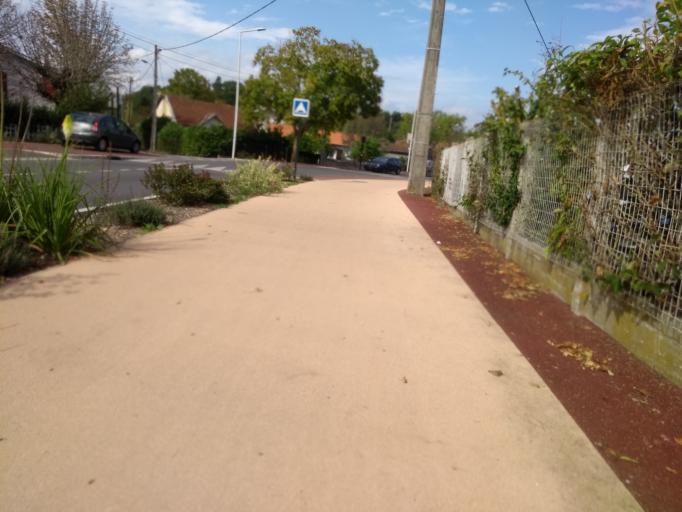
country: FR
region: Aquitaine
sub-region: Departement de la Gironde
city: Gradignan
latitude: 44.7737
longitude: -0.6211
